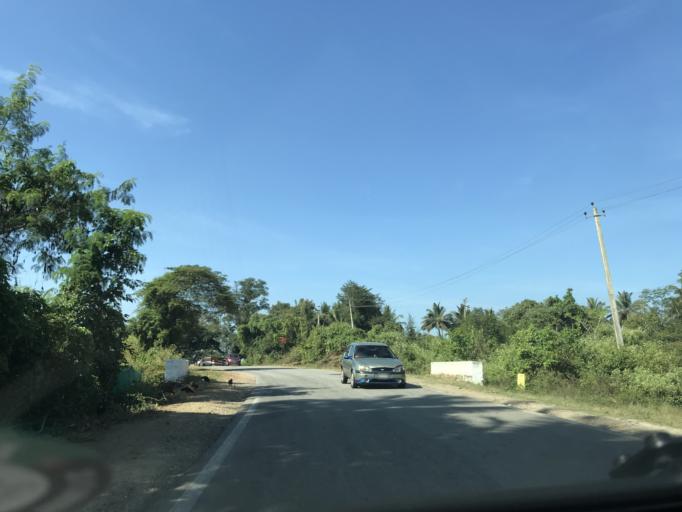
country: IN
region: Karnataka
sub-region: Mysore
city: Heggadadevankote
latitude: 12.1249
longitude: 76.4258
